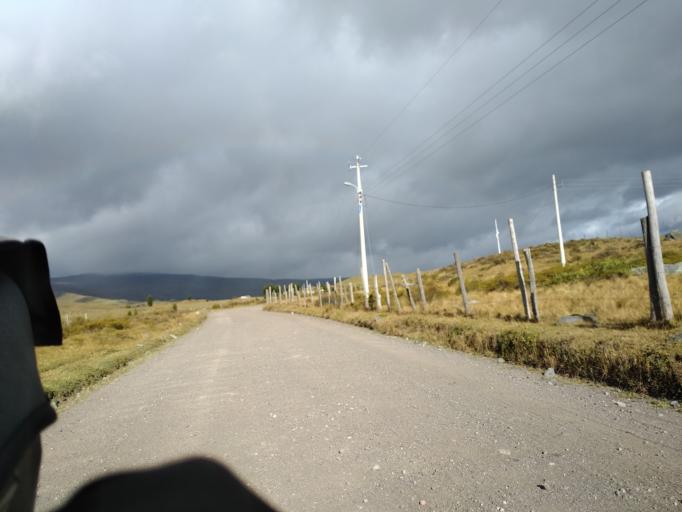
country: EC
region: Pichincha
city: Machachi
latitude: -0.5607
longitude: -78.4485
